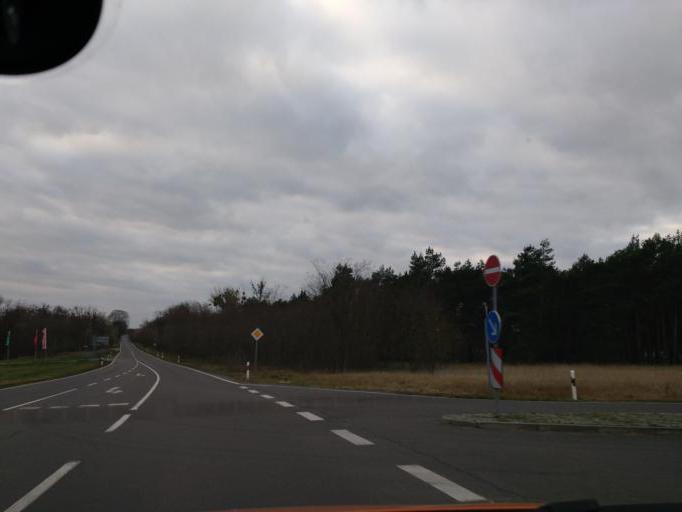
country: DE
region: Brandenburg
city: Wriezen
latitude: 52.7053
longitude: 14.1209
